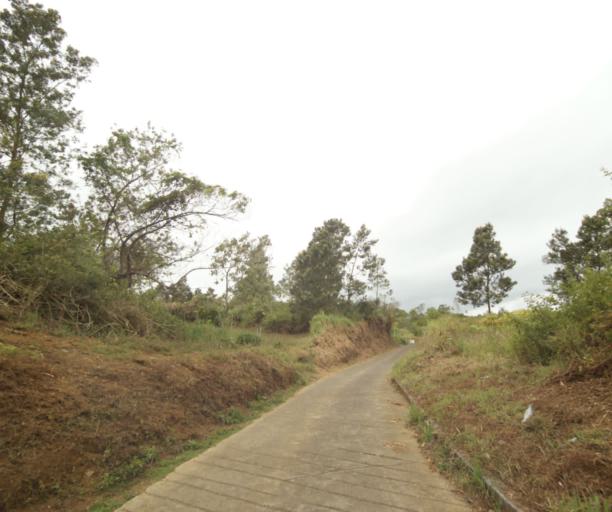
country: RE
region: Reunion
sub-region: Reunion
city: Saint-Paul
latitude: -21.0079
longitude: 55.3446
